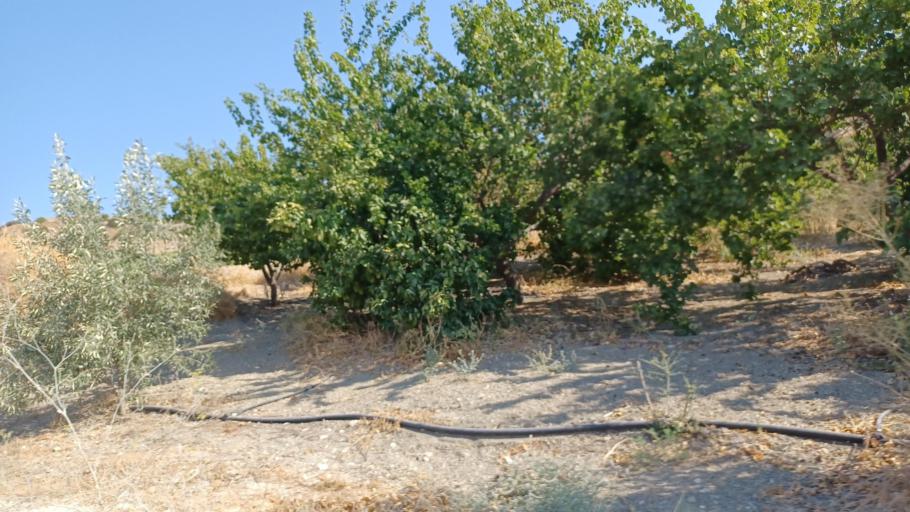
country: CY
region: Pafos
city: Polis
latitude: 34.9613
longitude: 32.4963
